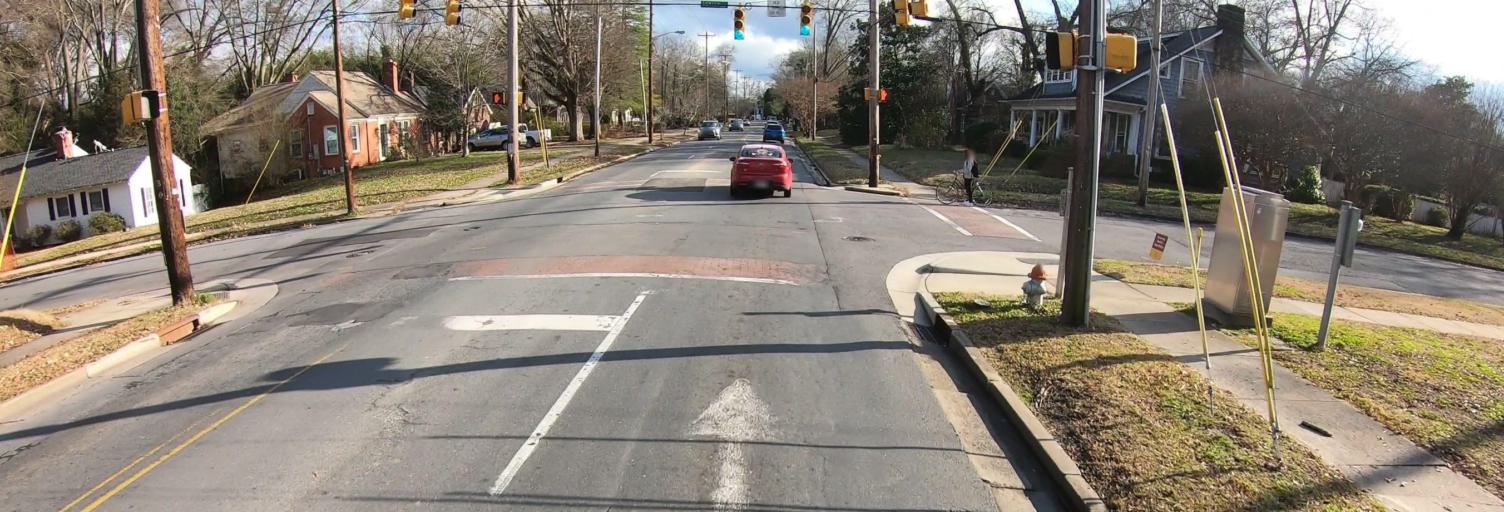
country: US
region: South Carolina
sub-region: York County
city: Rock Hill
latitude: 34.9396
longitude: -81.0262
